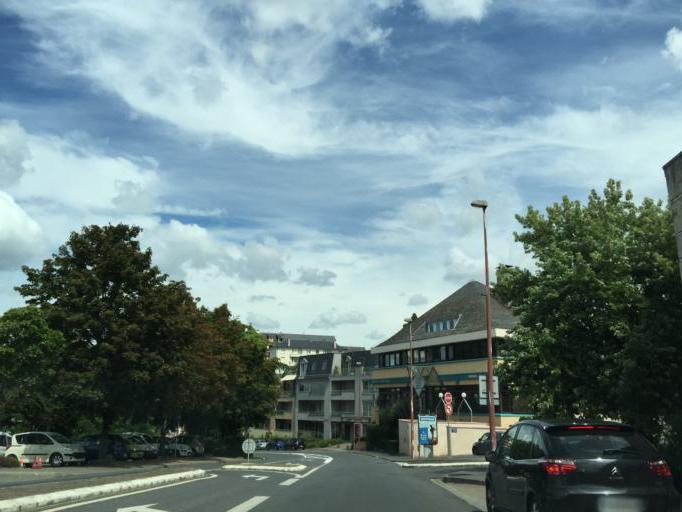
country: FR
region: Midi-Pyrenees
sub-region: Departement de l'Aveyron
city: Rodez
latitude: 44.3529
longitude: 2.5686
